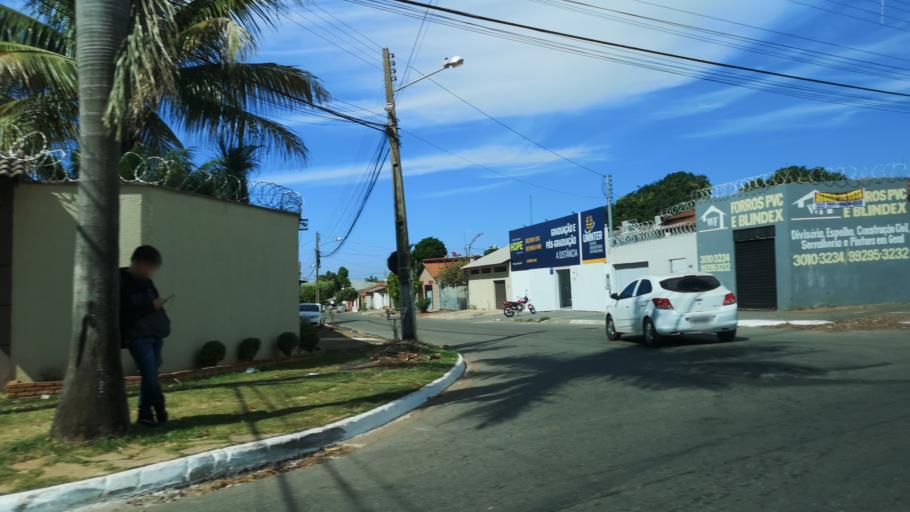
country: BR
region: Goias
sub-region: Senador Canedo
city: Senador Canedo
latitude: -16.6999
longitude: -49.1032
